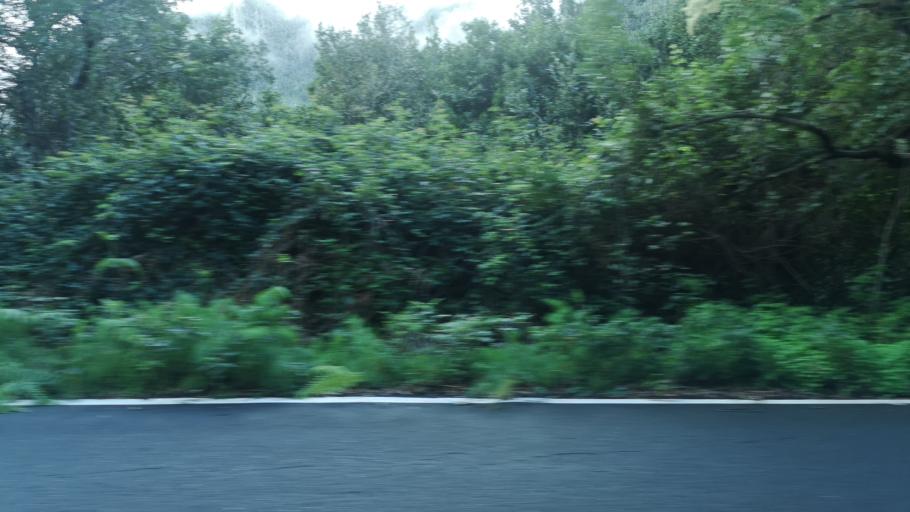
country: ES
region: Canary Islands
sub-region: Provincia de Santa Cruz de Tenerife
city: Hermigua
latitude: 28.1276
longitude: -17.2113
